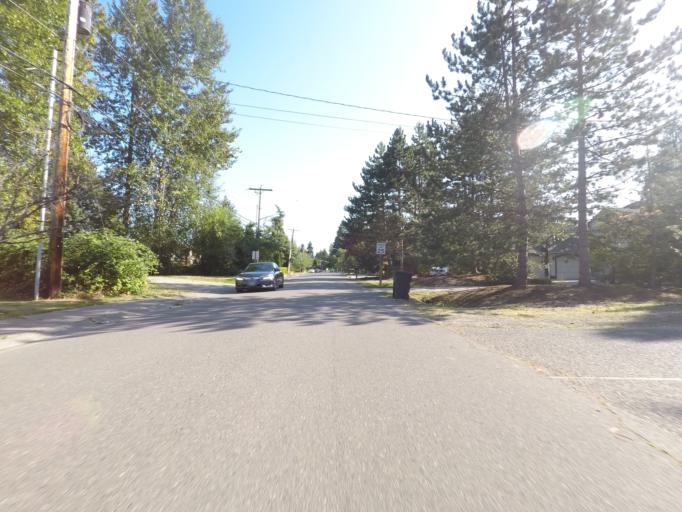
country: US
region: Washington
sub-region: King County
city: Inglewood-Finn Hill
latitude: 47.7366
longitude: -122.2373
